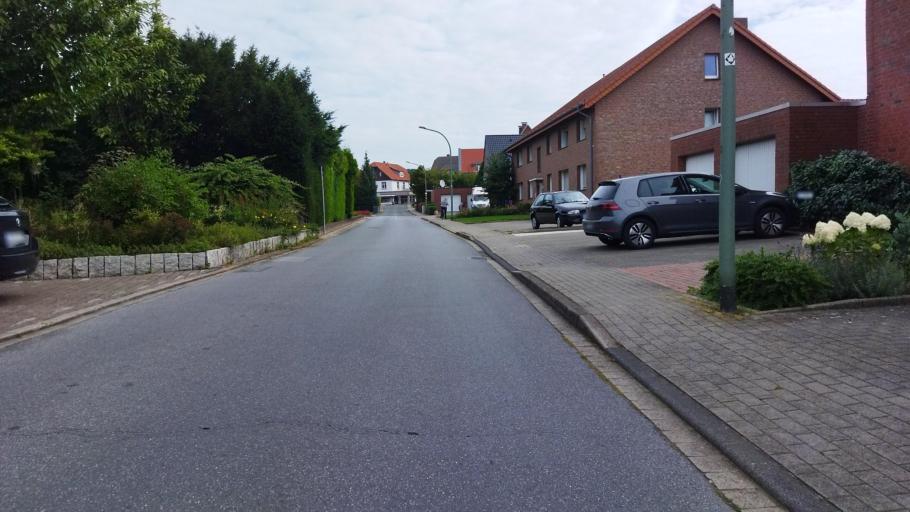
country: DE
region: Lower Saxony
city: Hilter
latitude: 52.1341
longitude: 8.1470
